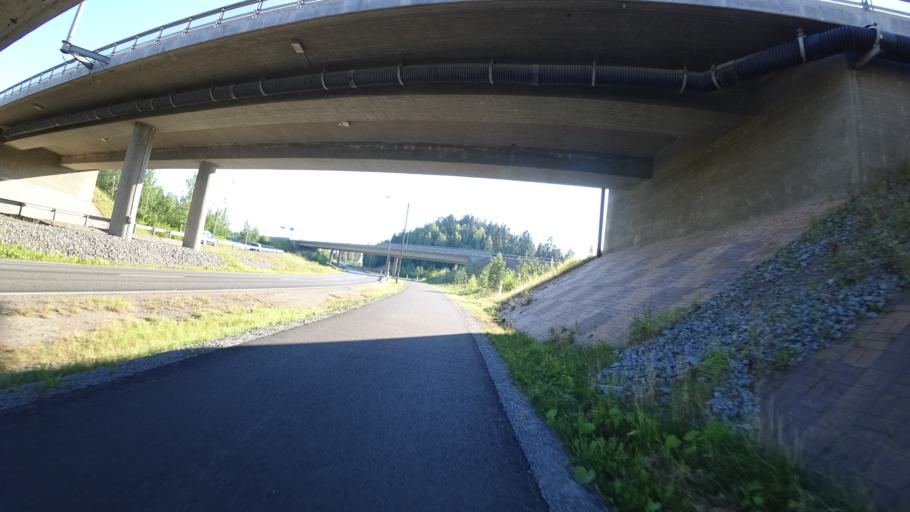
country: FI
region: Pirkanmaa
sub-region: Tampere
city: Pirkkala
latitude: 61.4898
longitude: 23.5838
